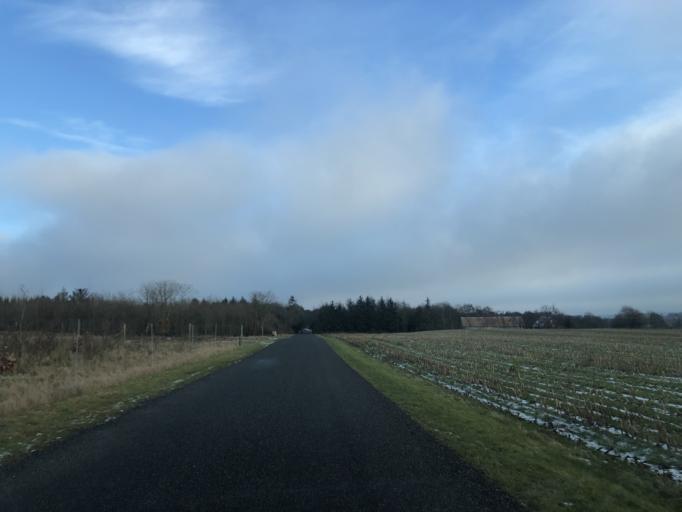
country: DK
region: Central Jutland
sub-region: Holstebro Kommune
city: Ulfborg
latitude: 56.2063
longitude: 8.3663
